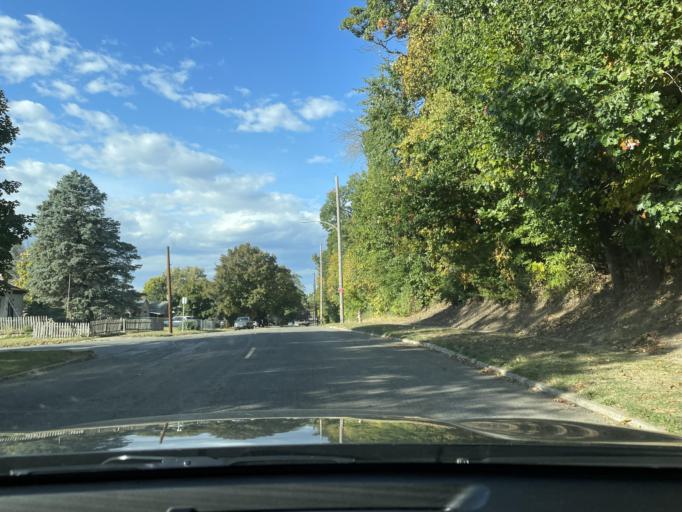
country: US
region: Missouri
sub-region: Buchanan County
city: Saint Joseph
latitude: 39.7786
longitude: -94.8342
